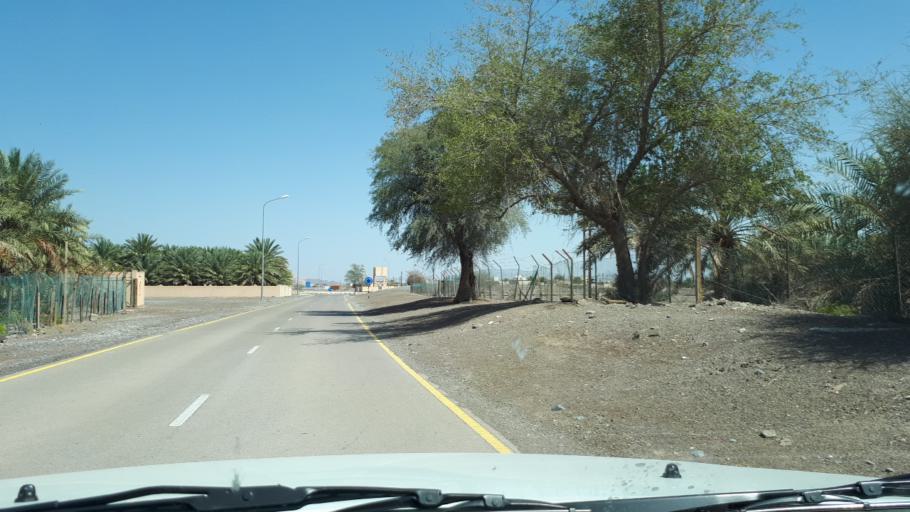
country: OM
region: Muhafazat ad Dakhiliyah
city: Bahla'
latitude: 22.9149
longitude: 57.2505
